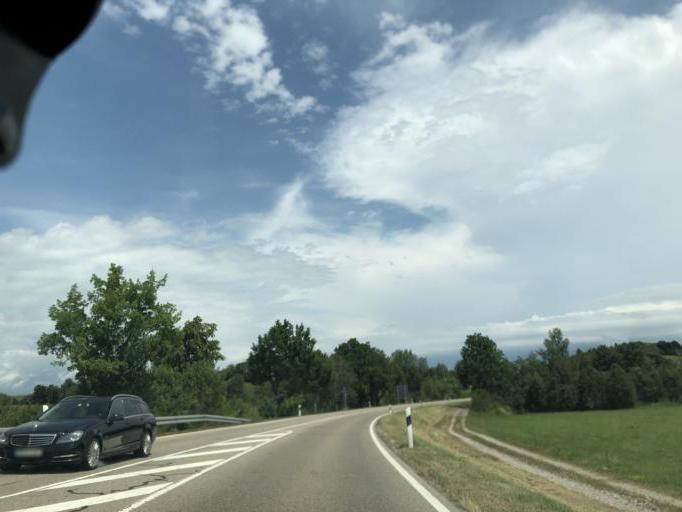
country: DE
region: Bavaria
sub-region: Swabia
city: Oy-Mittelberg
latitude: 47.6335
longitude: 10.4593
